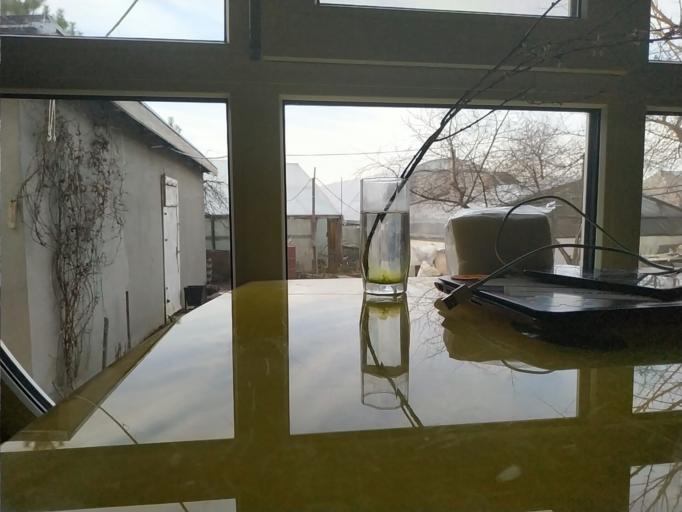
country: RU
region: Republic of Karelia
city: Suoyarvi
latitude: 61.8534
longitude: 32.2766
